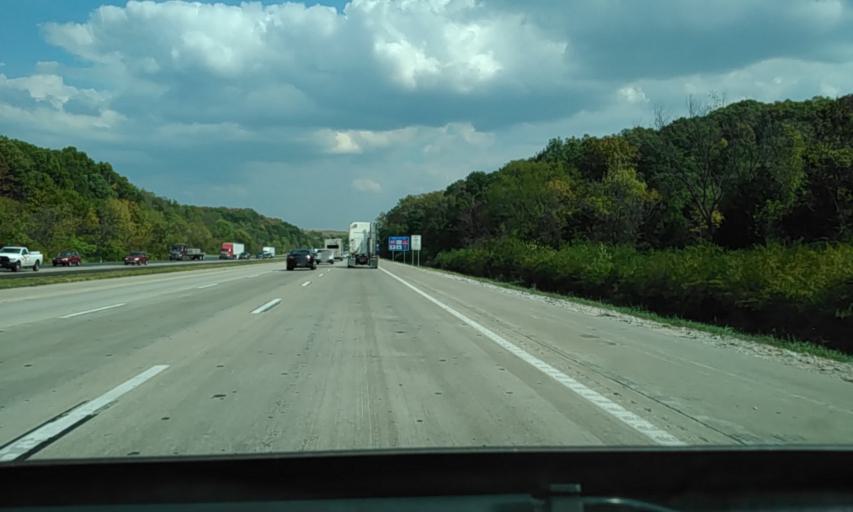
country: US
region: Missouri
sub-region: Saint Louis County
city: Valley Park
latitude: 38.5324
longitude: -90.5233
